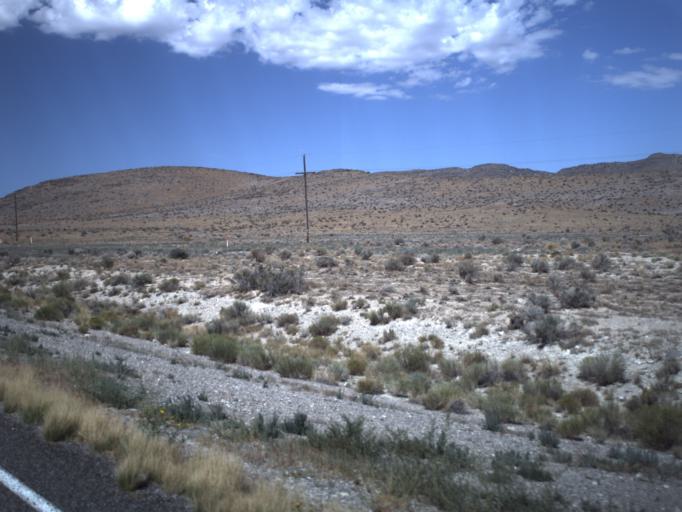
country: US
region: Utah
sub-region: Beaver County
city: Milford
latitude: 39.0600
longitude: -113.2471
